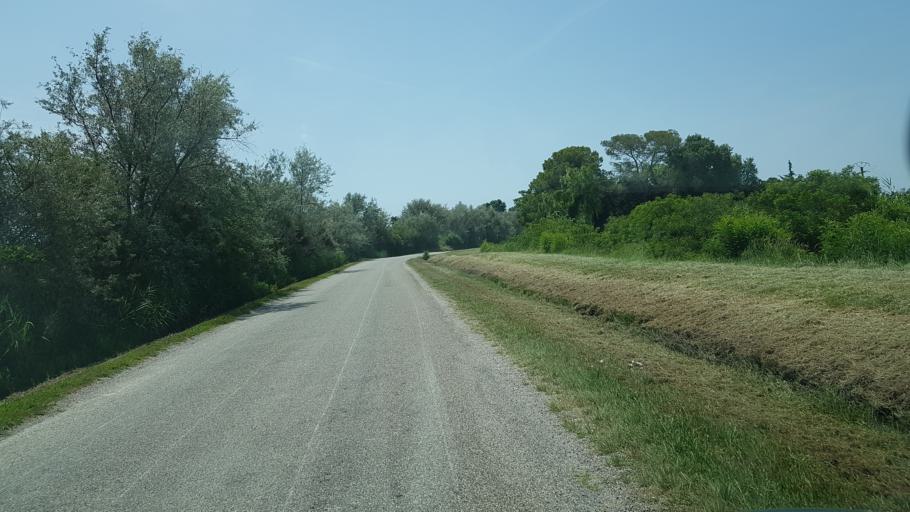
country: FR
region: Languedoc-Roussillon
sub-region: Departement du Gard
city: Saint-Gilles
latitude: 43.5756
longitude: 4.5045
